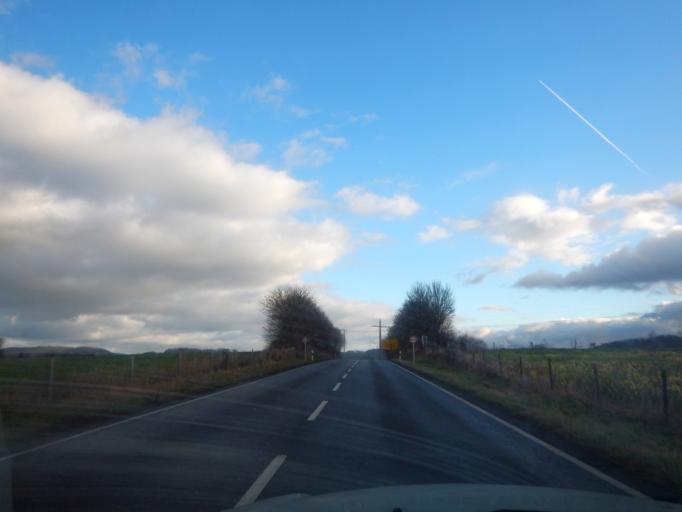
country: LU
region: Diekirch
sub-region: Canton de Redange
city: Useldange
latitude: 49.7570
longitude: 5.9562
